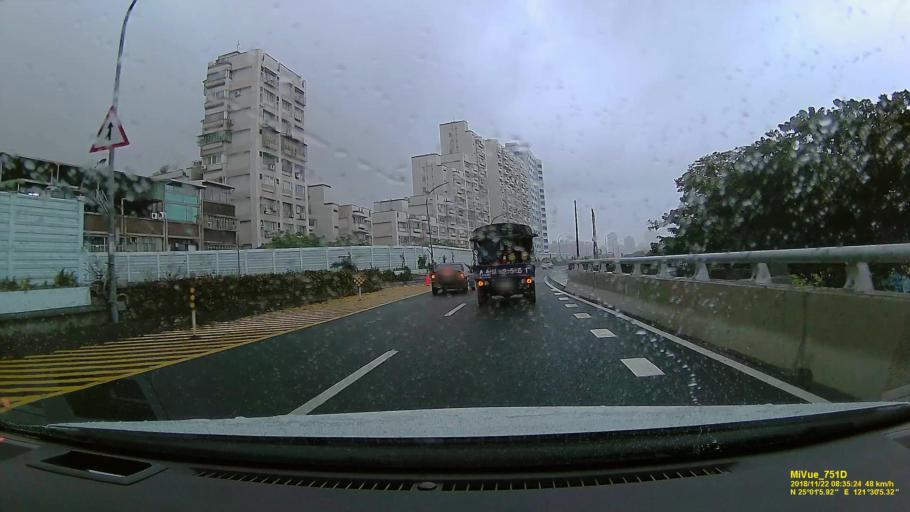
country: TW
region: Taipei
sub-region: Taipei
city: Banqiao
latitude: 25.0184
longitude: 121.5016
